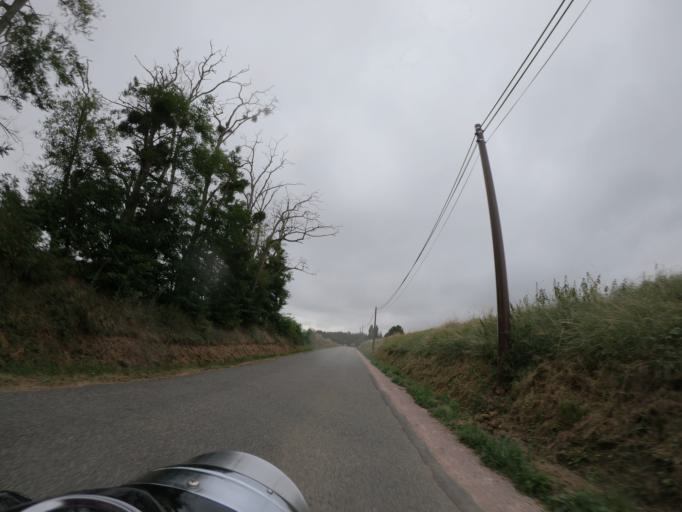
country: FR
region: Midi-Pyrenees
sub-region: Departement de l'Ariege
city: La Tour-du-Crieu
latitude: 43.0987
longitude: 1.7210
